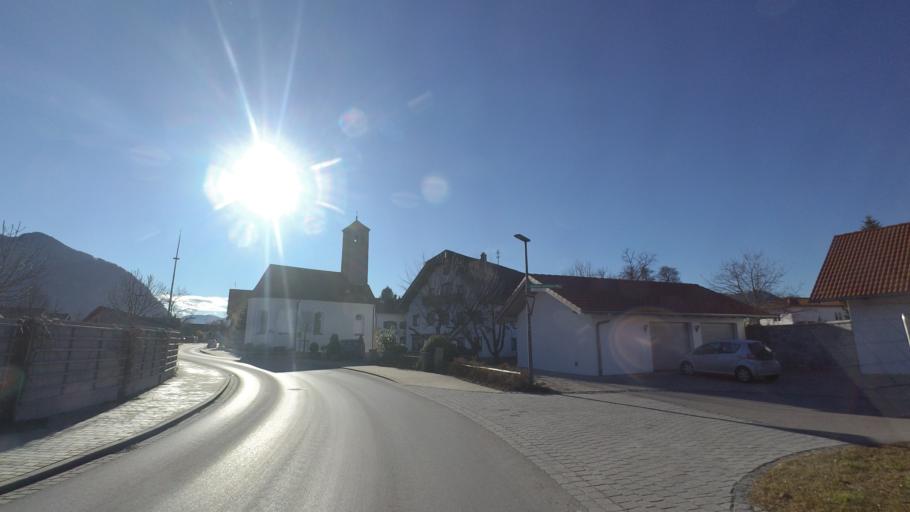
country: DE
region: Bavaria
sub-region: Upper Bavaria
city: Staudach-Egerndach
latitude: 47.7974
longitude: 12.4730
